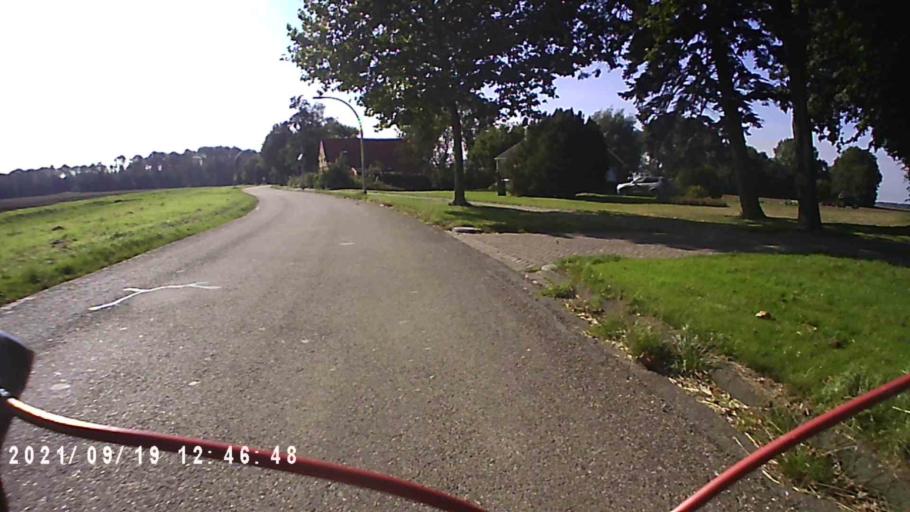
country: NL
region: Groningen
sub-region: Gemeente  Oldambt
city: Winschoten
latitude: 53.2146
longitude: 6.9420
